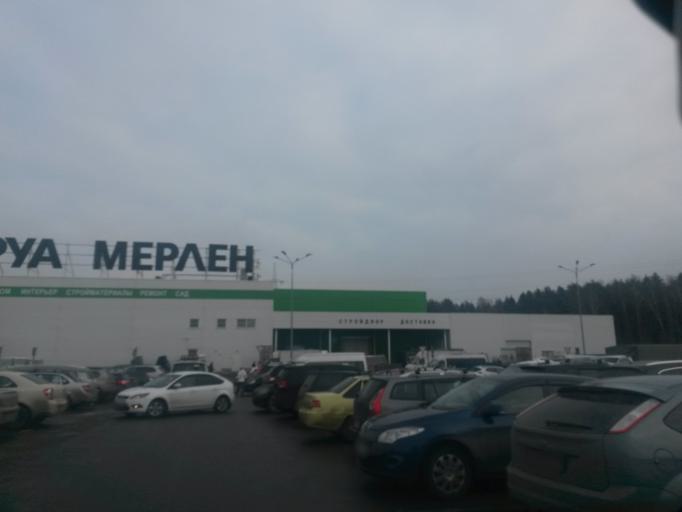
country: RU
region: Moskovskaya
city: Klimovsk
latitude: 55.3869
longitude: 37.5473
